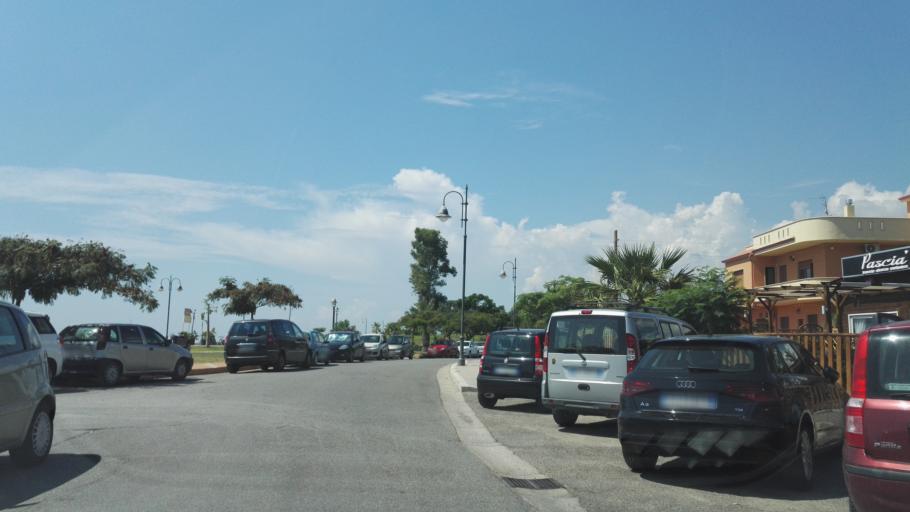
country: IT
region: Calabria
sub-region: Provincia di Reggio Calabria
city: Caulonia Marina
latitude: 38.3405
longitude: 16.4656
